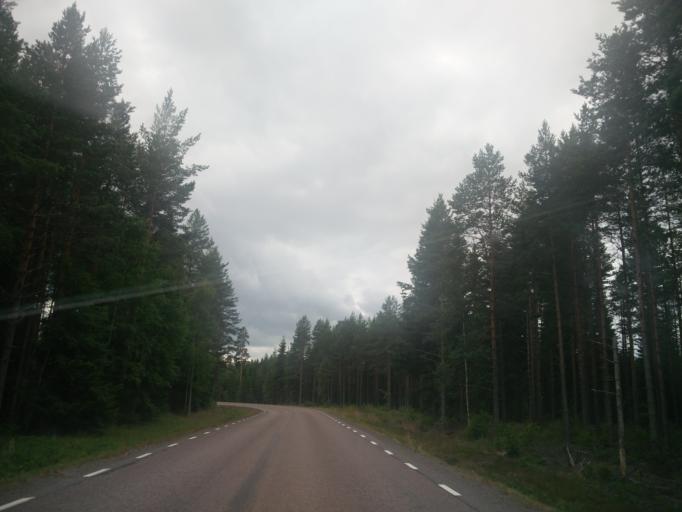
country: SE
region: Vaermland
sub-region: Arvika Kommun
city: Arvika
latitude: 59.9408
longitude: 12.6786
